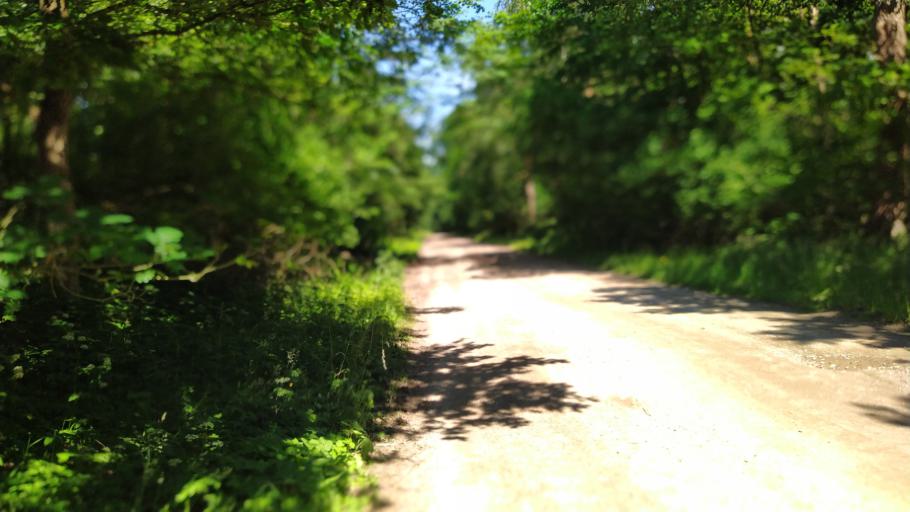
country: DE
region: Lower Saxony
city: Bargstedt
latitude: 53.4999
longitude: 9.4417
